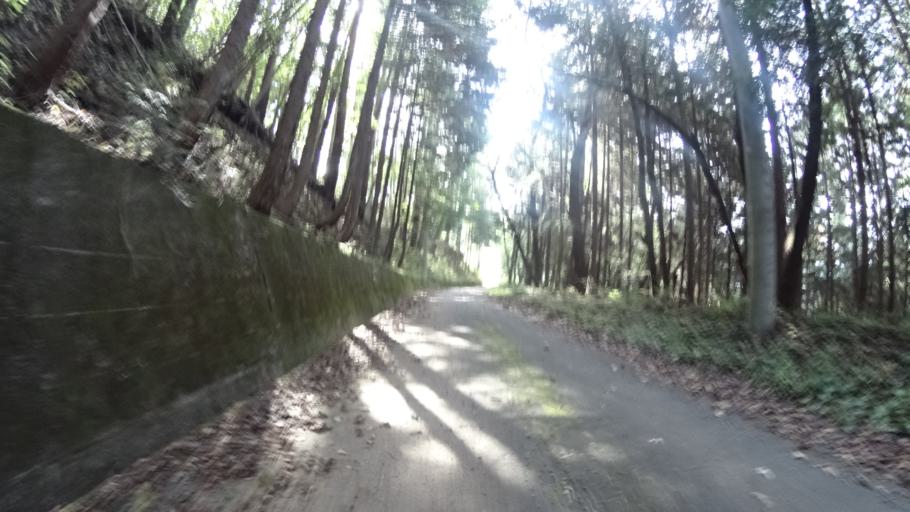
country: JP
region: Yamanashi
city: Otsuki
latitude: 35.5745
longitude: 138.9879
